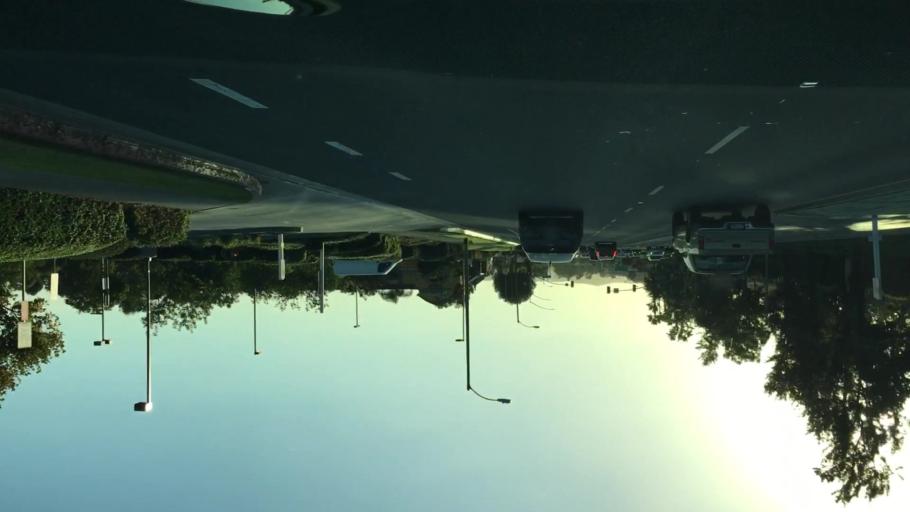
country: US
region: California
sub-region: Los Angeles County
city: Rowland Heights
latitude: 33.9903
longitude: -117.9191
